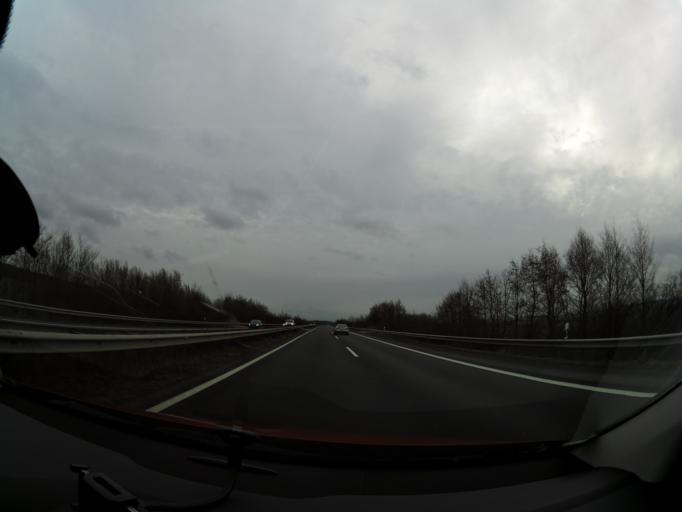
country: DE
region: Lower Saxony
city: Flothe
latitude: 52.0920
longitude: 10.4945
